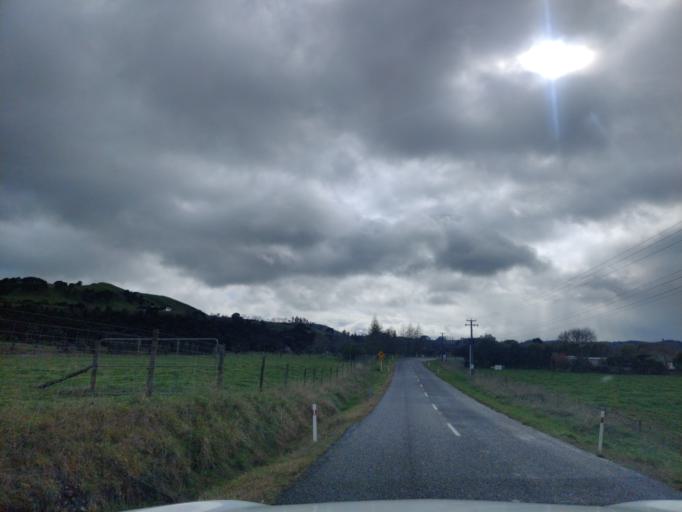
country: NZ
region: Manawatu-Wanganui
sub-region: Palmerston North City
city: Palmerston North
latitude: -40.1891
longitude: 175.7818
